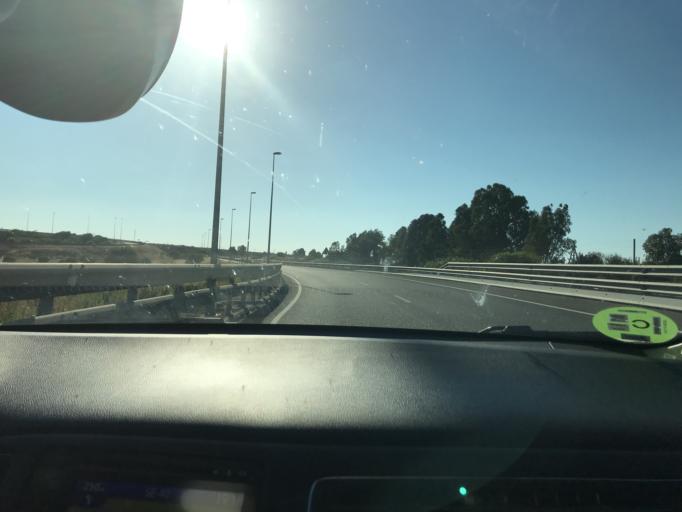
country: ES
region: Andalusia
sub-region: Provincia de Sevilla
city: Alcala de Guadaira
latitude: 37.4330
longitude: -5.8396
